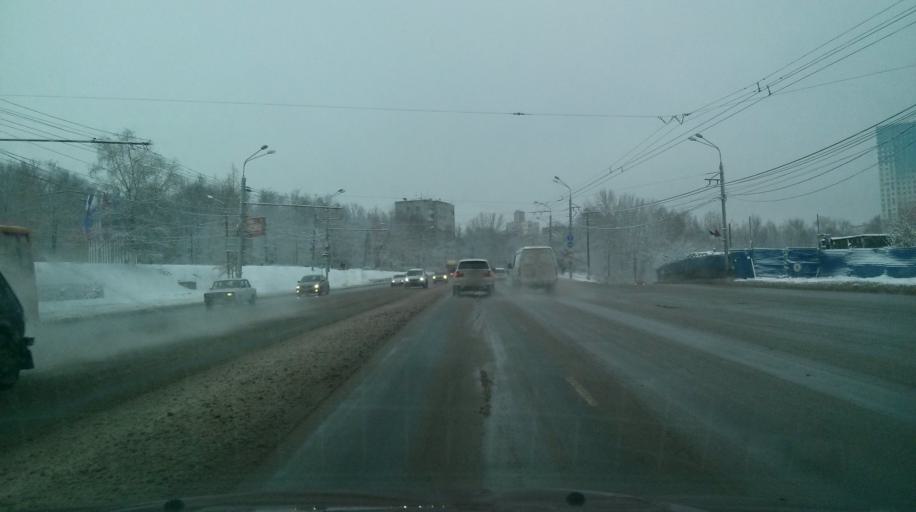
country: RU
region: Nizjnij Novgorod
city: Nizhniy Novgorod
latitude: 56.2436
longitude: 43.9646
